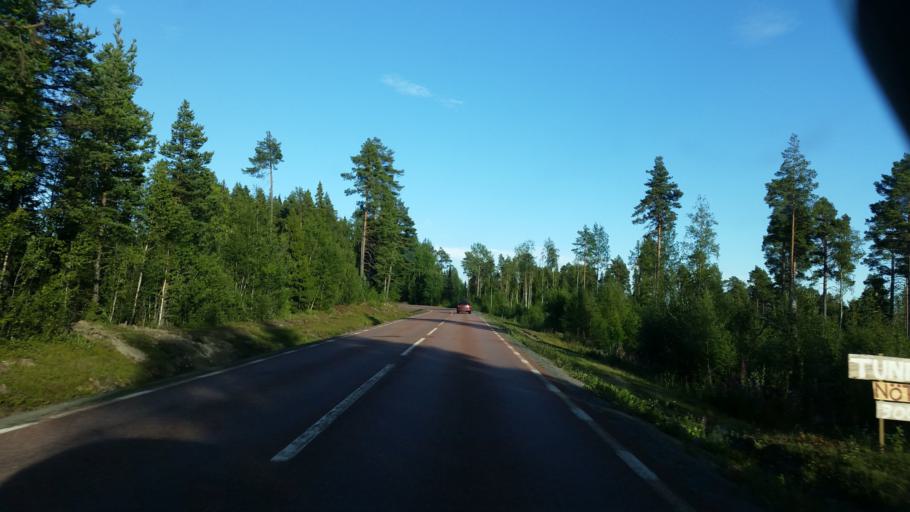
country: SE
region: Vaesterbotten
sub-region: Dorotea Kommun
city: Dorotea
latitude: 64.0666
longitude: 16.0659
